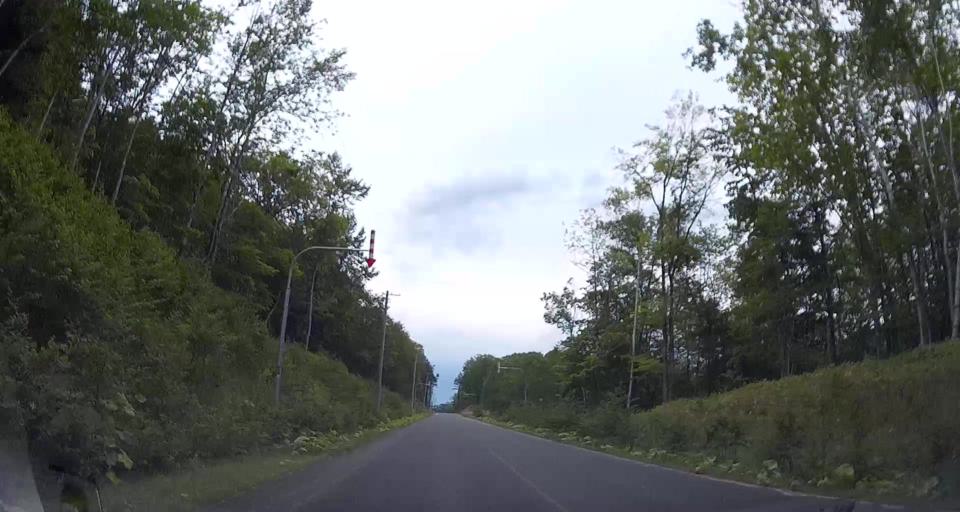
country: JP
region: Hokkaido
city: Chitose
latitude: 42.7810
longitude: 142.0161
